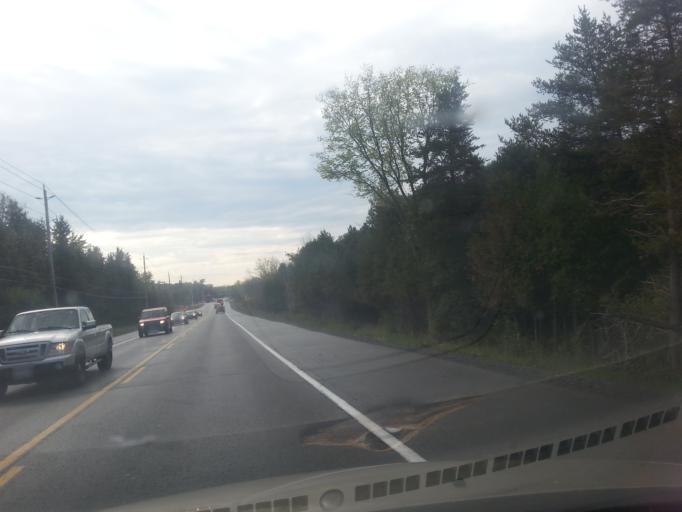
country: CA
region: Ontario
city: Bells Corners
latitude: 45.3064
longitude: -75.8180
